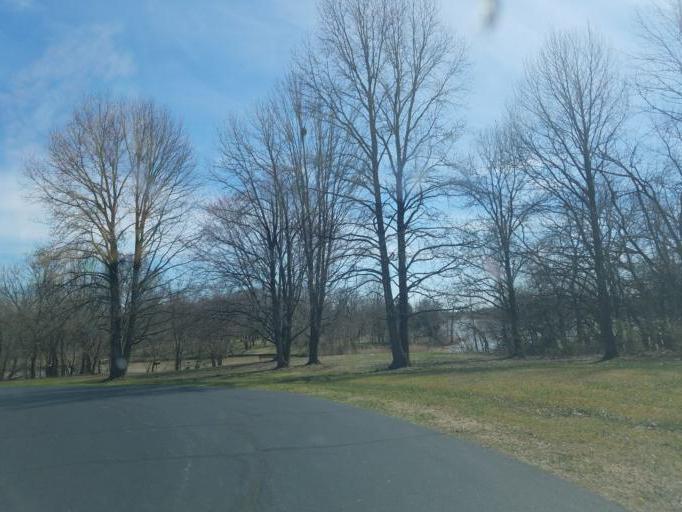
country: US
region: Ohio
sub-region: Delaware County
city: Delaware
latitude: 40.3686
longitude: -83.0673
